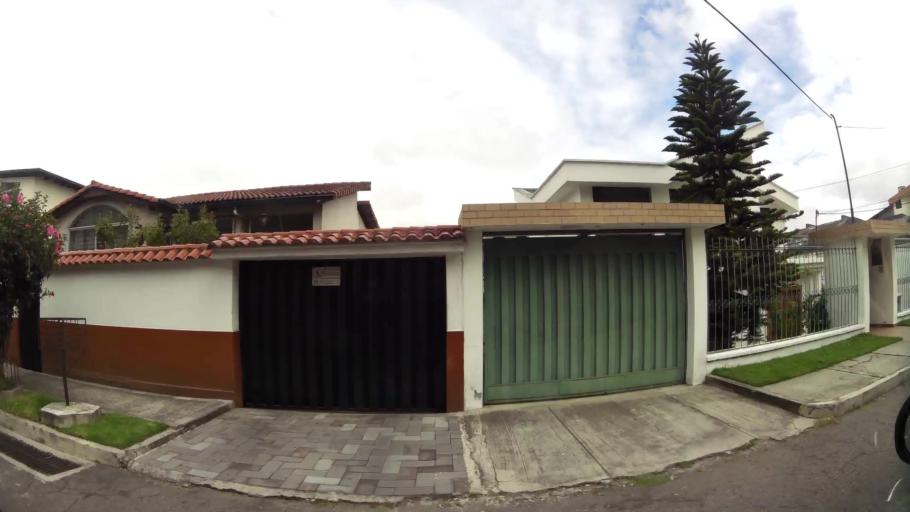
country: EC
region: Pichincha
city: Quito
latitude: -0.1780
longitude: -78.4745
